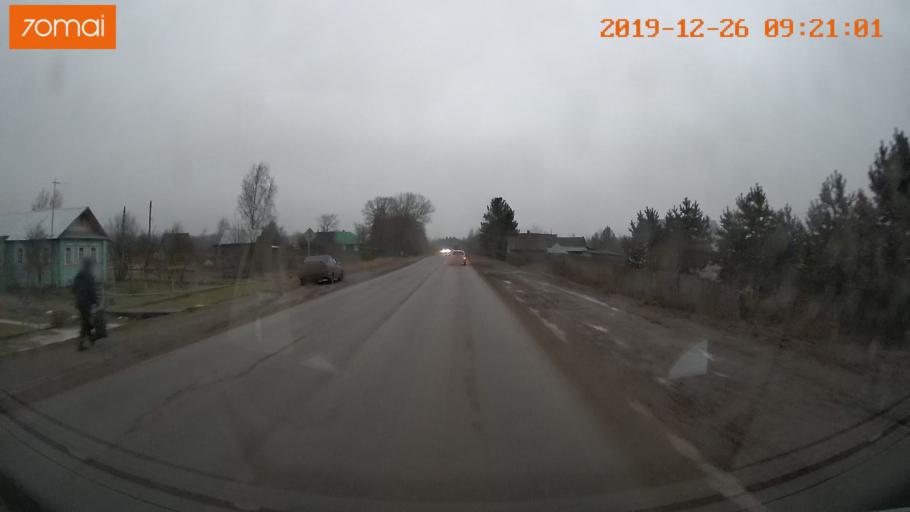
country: RU
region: Vologda
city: Gryazovets
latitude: 58.9666
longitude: 40.2268
